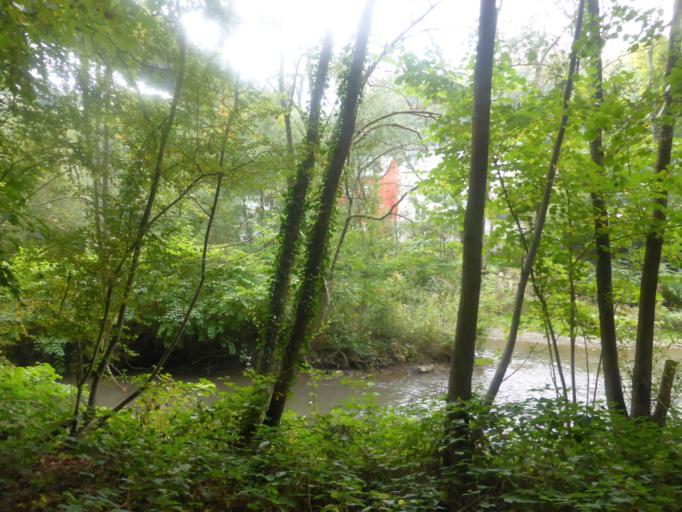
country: LU
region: Luxembourg
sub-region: Canton de Luxembourg
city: Hesperange
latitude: 49.5794
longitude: 6.1533
